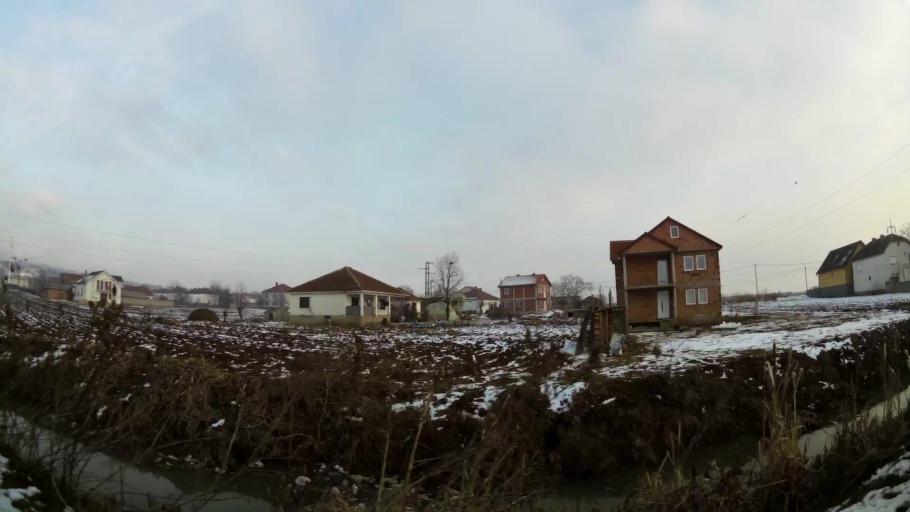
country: MK
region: Aracinovo
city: Arachinovo
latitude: 42.0197
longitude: 21.5599
